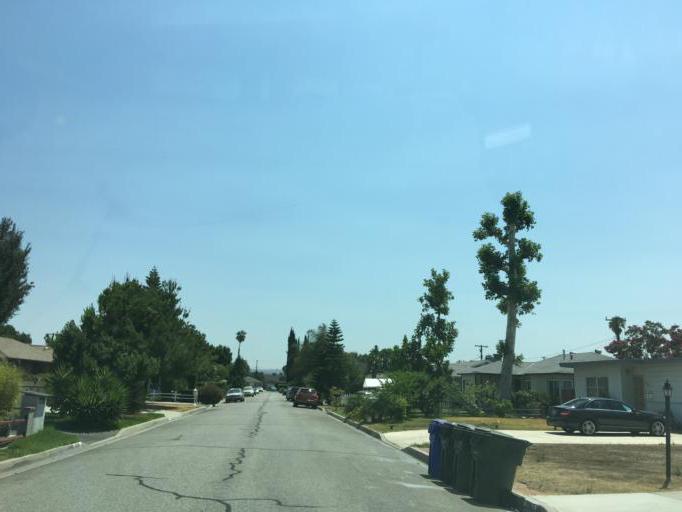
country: US
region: California
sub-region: Los Angeles County
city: Mayflower Village
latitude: 34.1127
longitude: -118.0140
